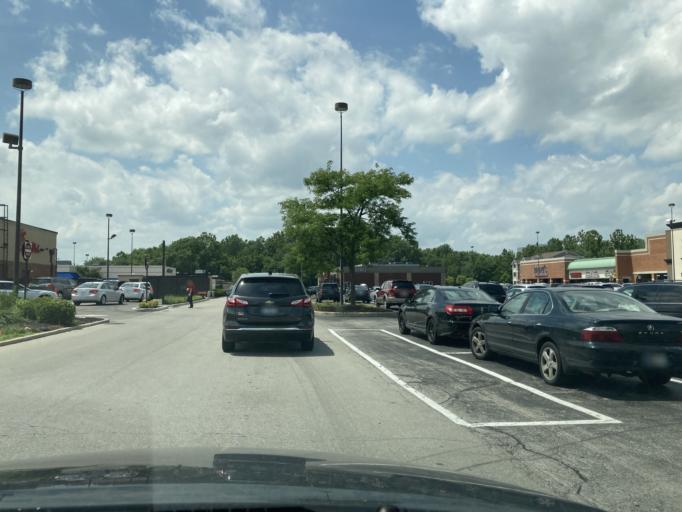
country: US
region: Indiana
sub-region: Marion County
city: Broad Ripple
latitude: 39.9096
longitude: -86.1010
